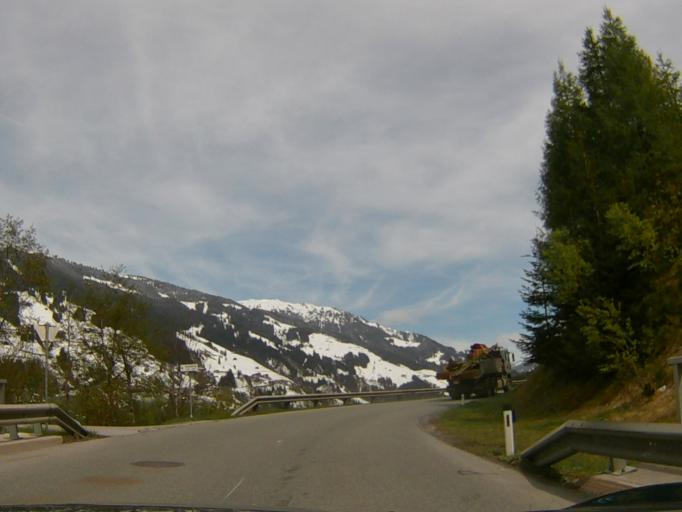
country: AT
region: Tyrol
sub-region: Politischer Bezirk Schwaz
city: Hainzenberg
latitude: 47.2149
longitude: 11.9106
